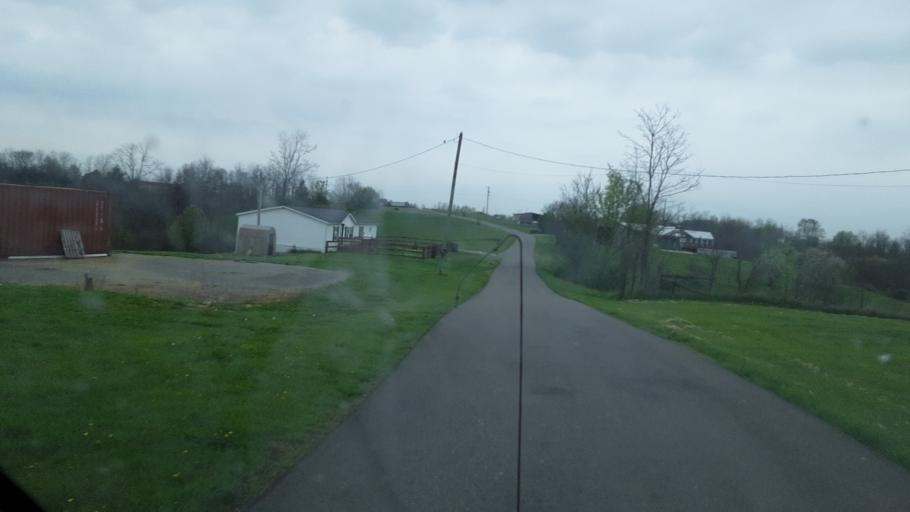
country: US
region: Kentucky
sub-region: Owen County
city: Owenton
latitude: 38.6707
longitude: -84.7831
